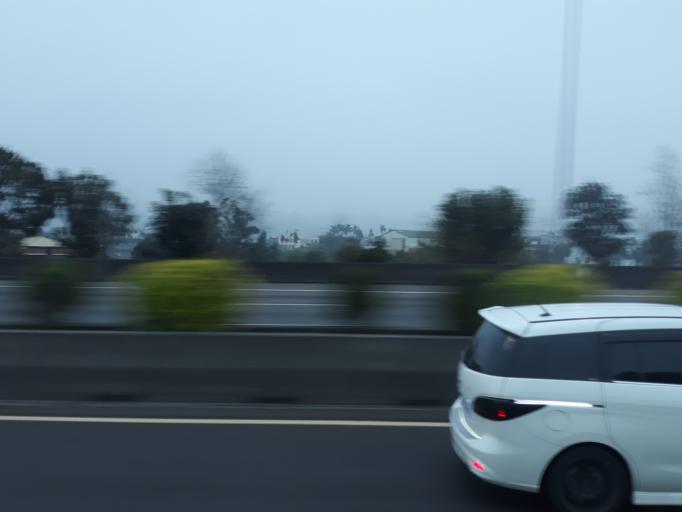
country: TW
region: Taiwan
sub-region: Miaoli
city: Miaoli
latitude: 24.5304
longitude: 120.8269
